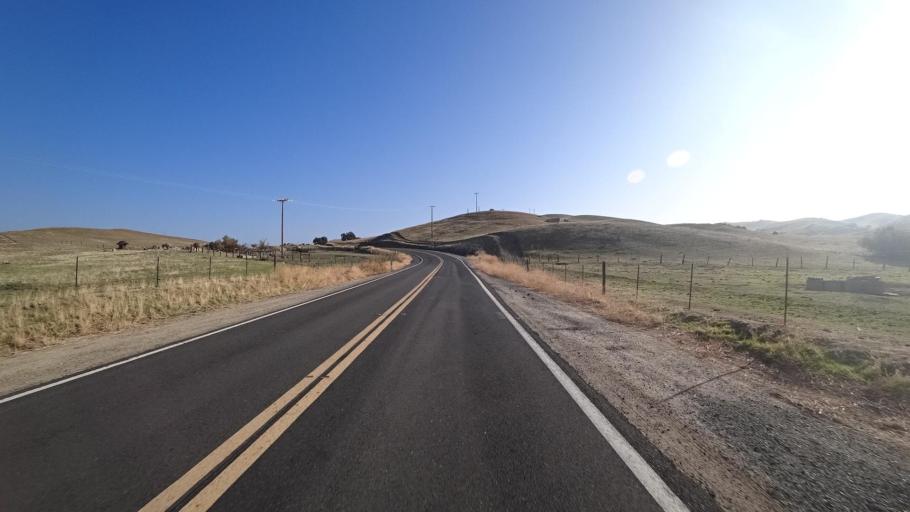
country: US
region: California
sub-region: Tulare County
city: Richgrove
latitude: 35.7417
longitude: -118.8853
